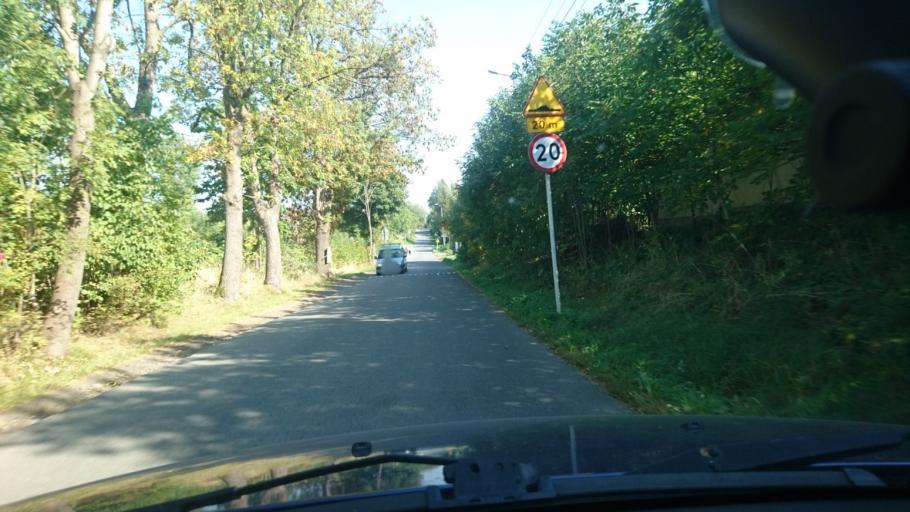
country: PL
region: Silesian Voivodeship
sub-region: Bielsko-Biala
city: Bielsko-Biala
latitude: 49.8575
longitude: 19.0542
